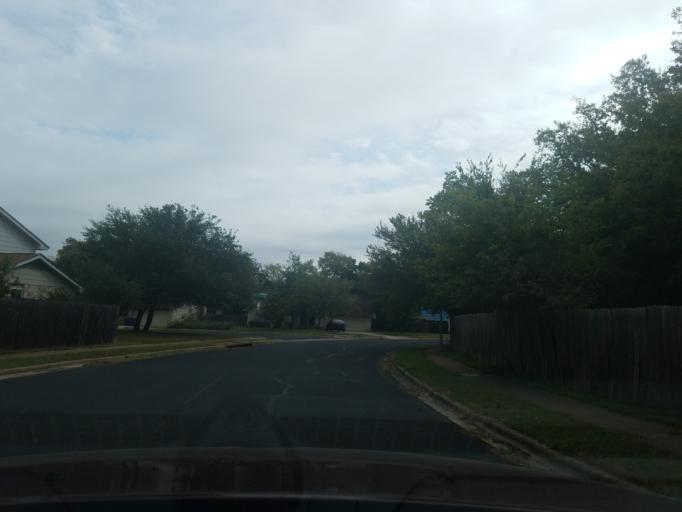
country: US
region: Texas
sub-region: Williamson County
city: Anderson Mill
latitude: 30.4636
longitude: -97.8060
